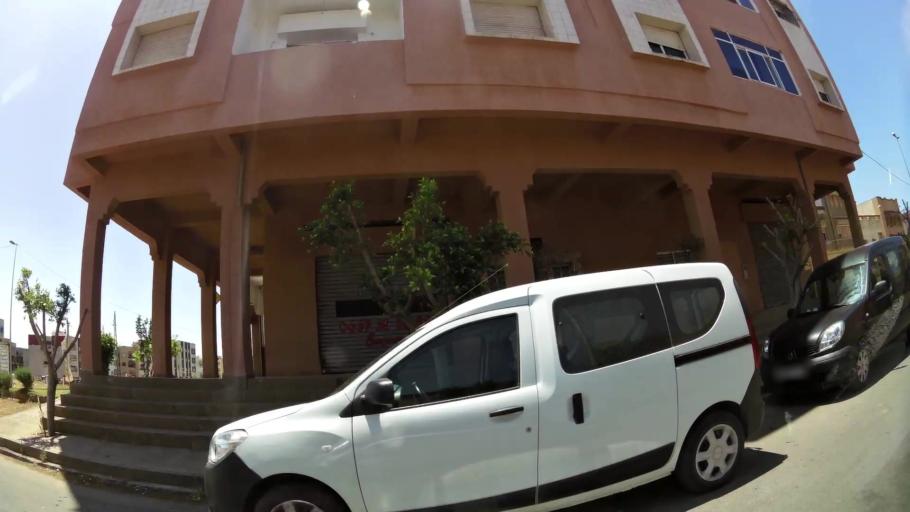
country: MA
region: Gharb-Chrarda-Beni Hssen
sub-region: Kenitra Province
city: Kenitra
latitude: 34.2540
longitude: -6.6206
